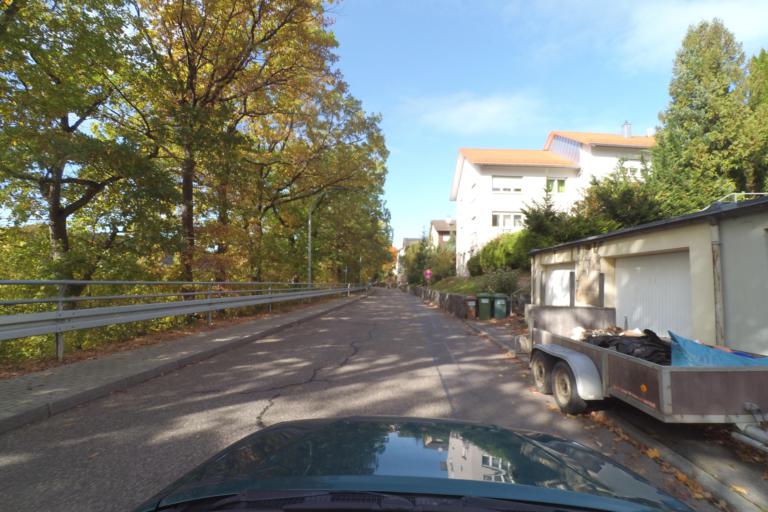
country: DE
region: Baden-Wuerttemberg
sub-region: Karlsruhe Region
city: Nagold
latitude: 48.5632
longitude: 8.7270
